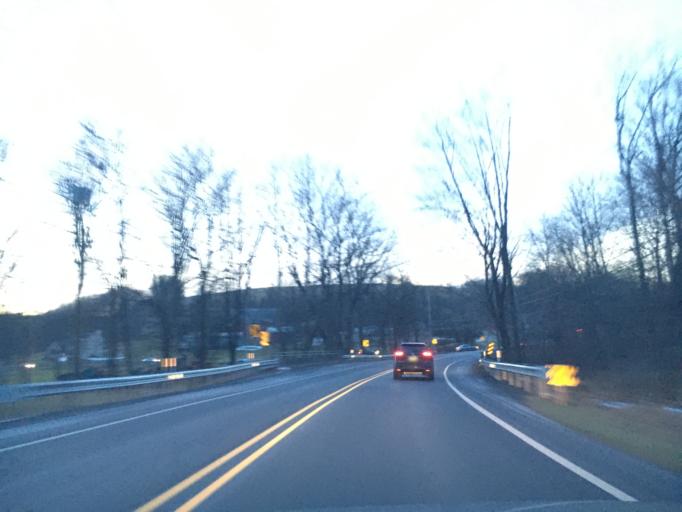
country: US
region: Pennsylvania
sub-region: Northampton County
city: Cherryville
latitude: 40.7471
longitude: -75.5094
